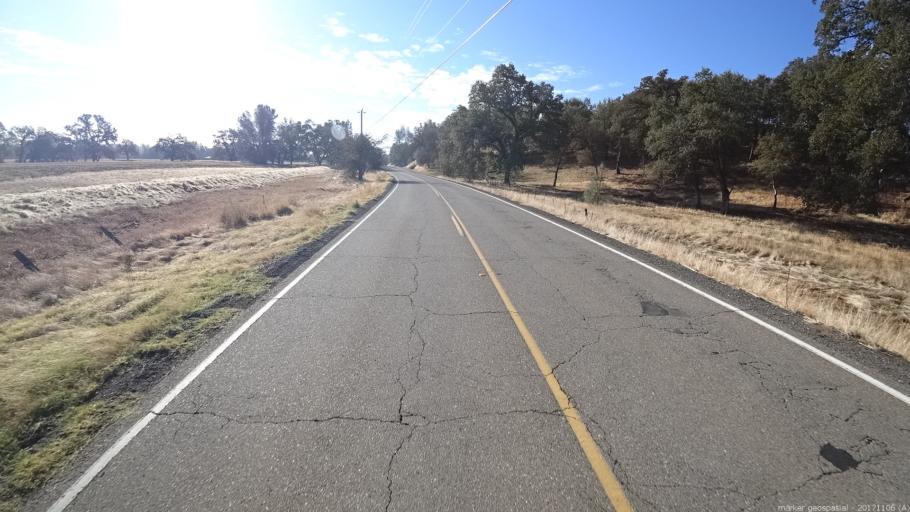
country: US
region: California
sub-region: Shasta County
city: Palo Cedro
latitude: 40.5046
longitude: -122.2384
